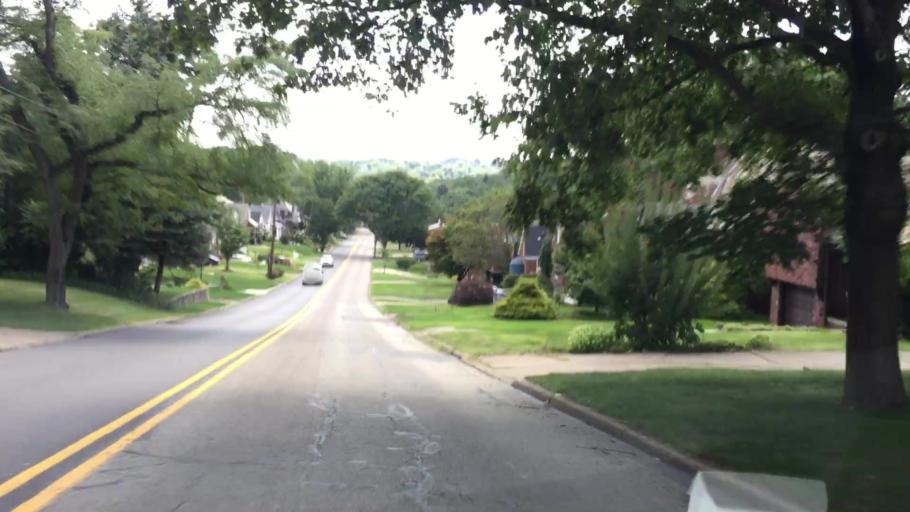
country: US
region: Pennsylvania
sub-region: Allegheny County
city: Heidelberg
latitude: 40.3713
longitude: -80.0774
